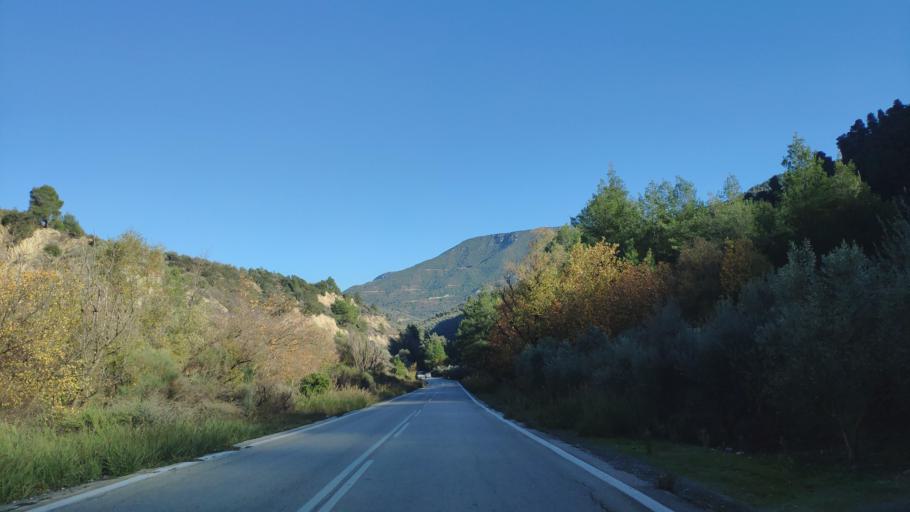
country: GR
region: Peloponnese
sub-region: Nomos Korinthias
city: Xylokastro
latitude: 38.0091
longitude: 22.5250
